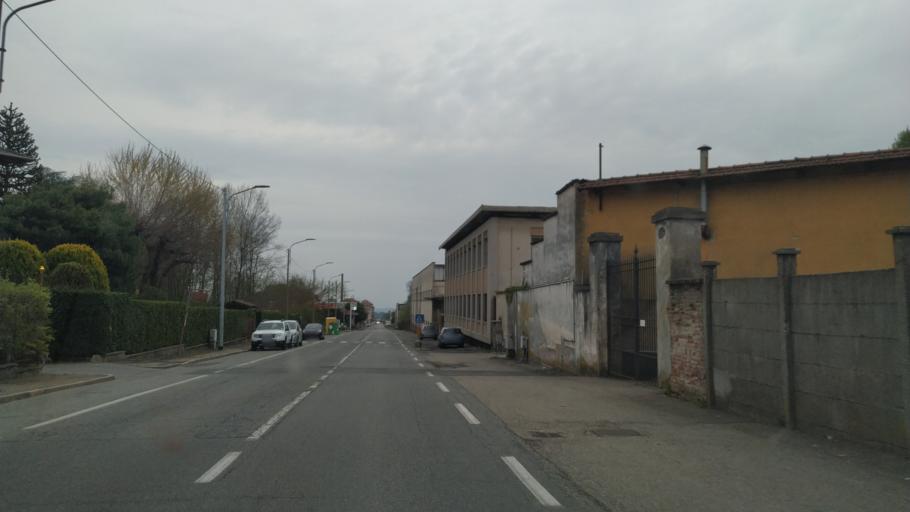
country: IT
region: Piedmont
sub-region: Provincia di Biella
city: Occhieppo Inferiore
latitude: 45.5627
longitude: 8.0236
